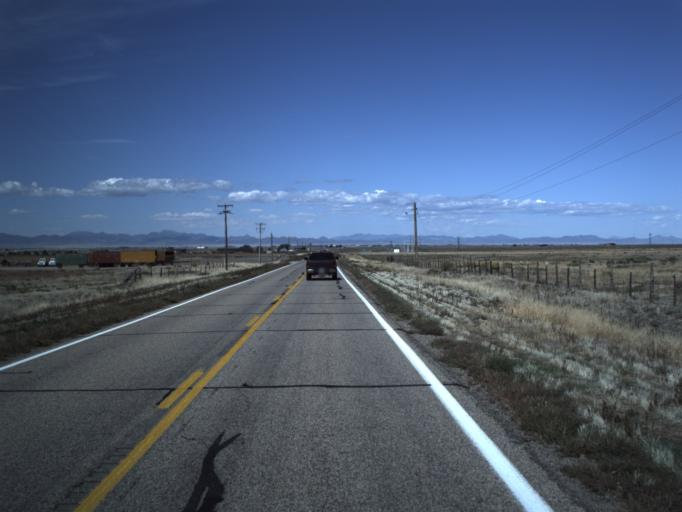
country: US
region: Utah
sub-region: Washington County
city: Enterprise
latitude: 37.6031
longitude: -113.6612
